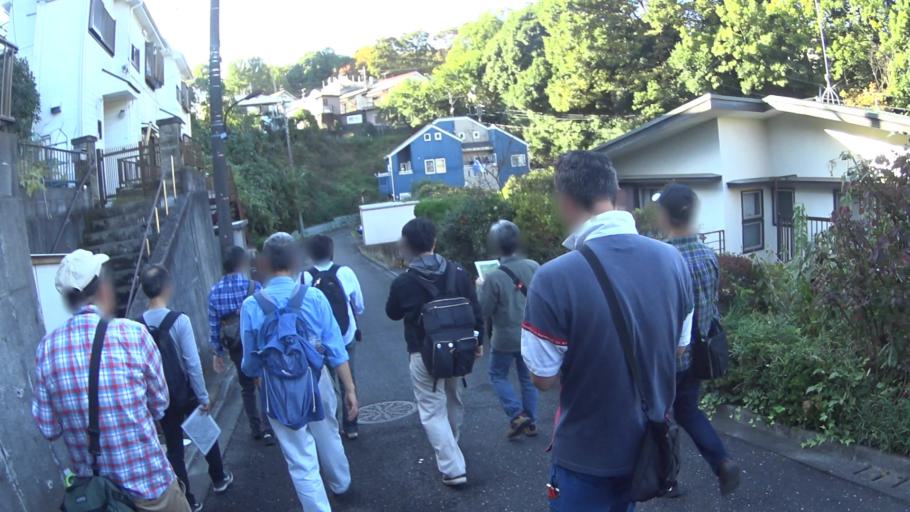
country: JP
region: Tokyo
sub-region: Machida-shi
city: Machida
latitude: 35.5789
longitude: 139.4420
